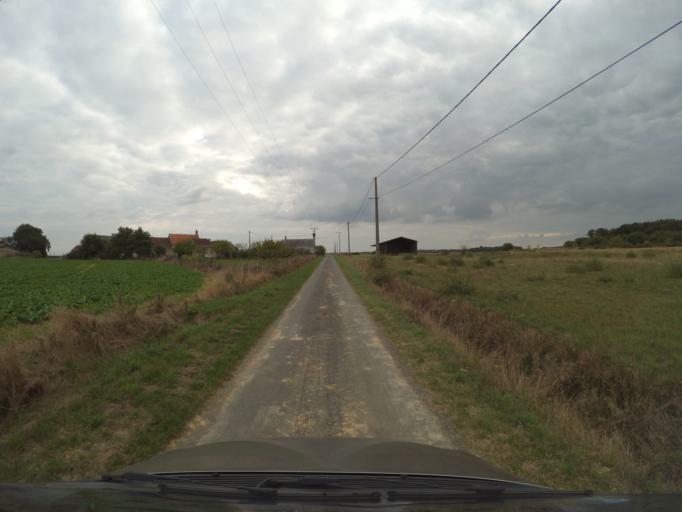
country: FR
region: Centre
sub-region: Departement d'Indre-et-Loire
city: Reugny
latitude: 47.4821
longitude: 0.9260
